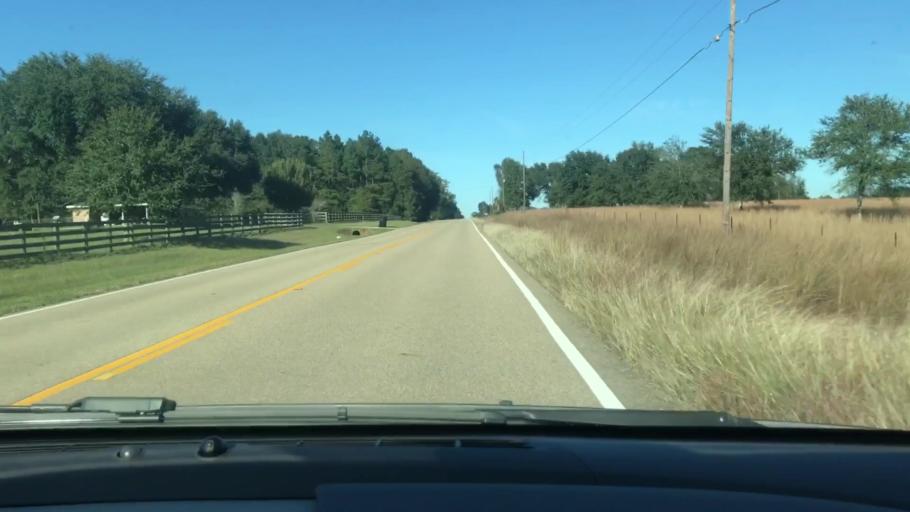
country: US
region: Louisiana
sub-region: Saint Tammany Parish
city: Abita Springs
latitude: 30.6055
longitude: -90.0284
